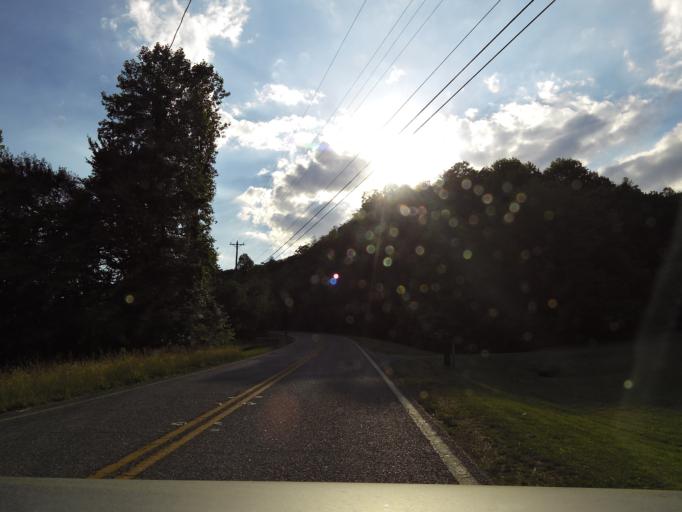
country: US
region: Georgia
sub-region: Union County
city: Blairsville
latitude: 34.7999
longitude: -83.8671
